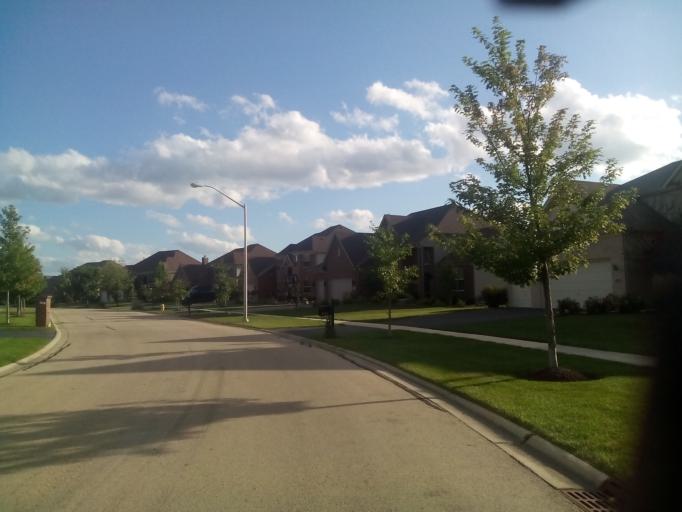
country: US
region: Illinois
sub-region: Will County
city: Romeoville
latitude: 41.6876
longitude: -88.1557
